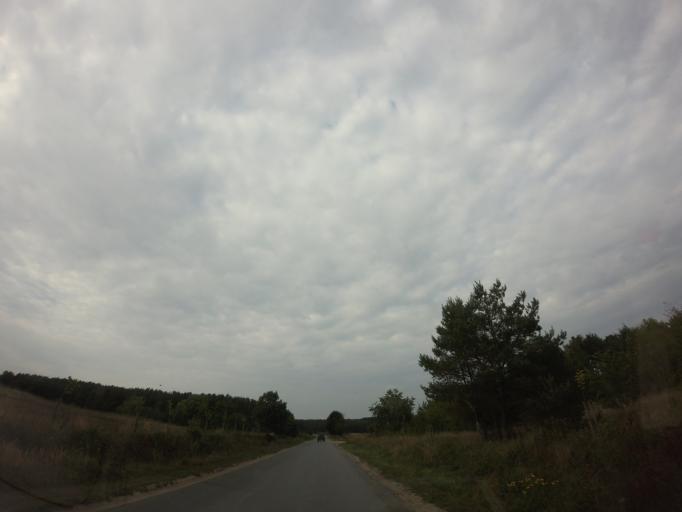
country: PL
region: West Pomeranian Voivodeship
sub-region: Powiat drawski
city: Drawsko Pomorskie
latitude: 53.5002
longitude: 15.7844
